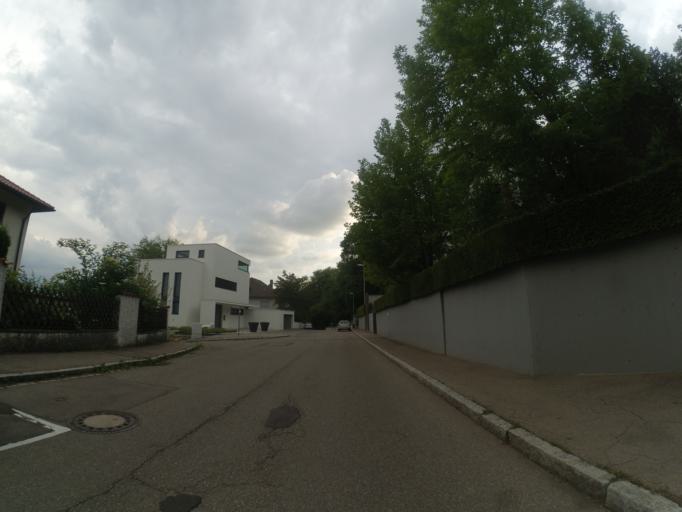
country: DE
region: Baden-Wuerttemberg
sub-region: Tuebingen Region
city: Ulm
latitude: 48.4100
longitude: 9.9826
